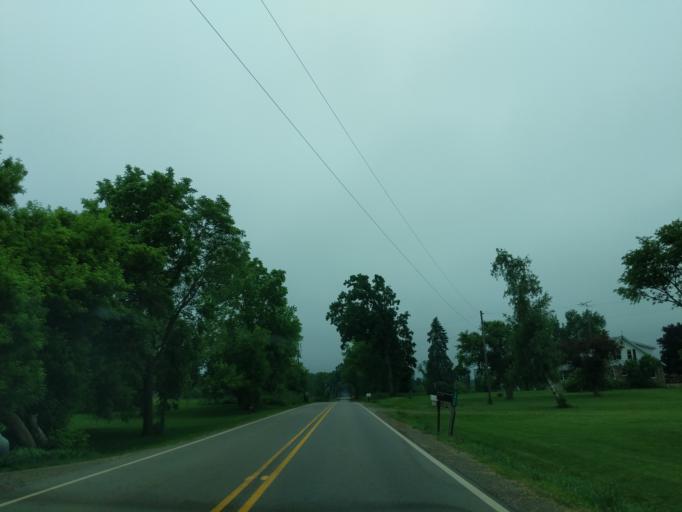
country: US
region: Michigan
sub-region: Jackson County
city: Spring Arbor
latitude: 42.2062
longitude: -84.5700
